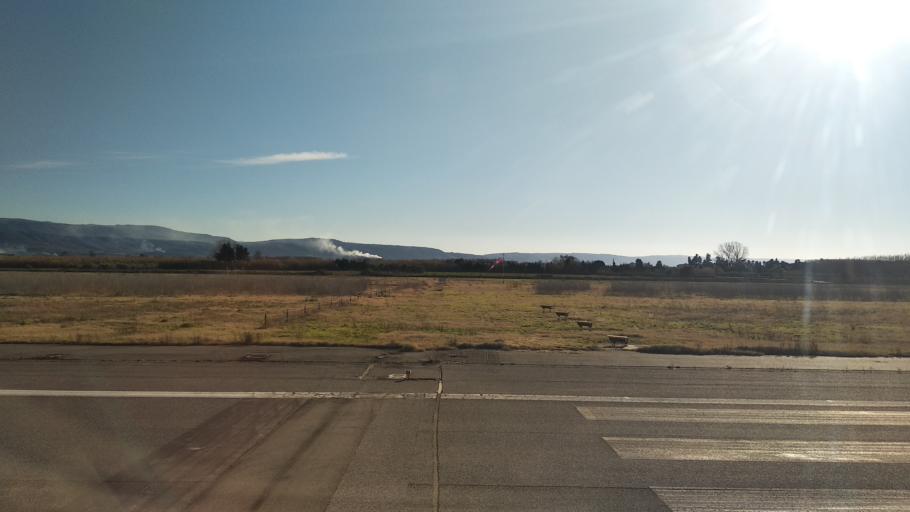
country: IT
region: Calabria
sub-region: Provincia di Catanzaro
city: Santa Eufemia Lamezia
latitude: 38.9039
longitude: 16.2548
